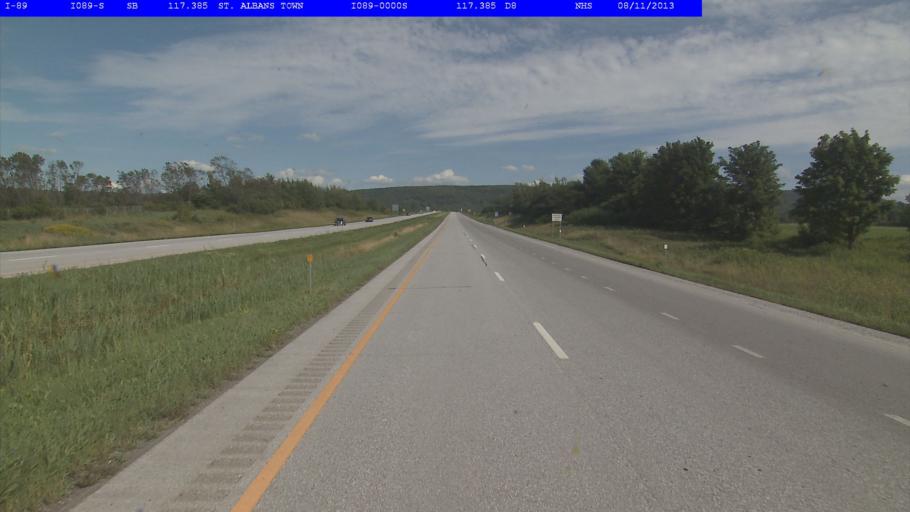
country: US
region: Vermont
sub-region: Franklin County
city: Saint Albans
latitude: 44.8418
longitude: -73.0755
